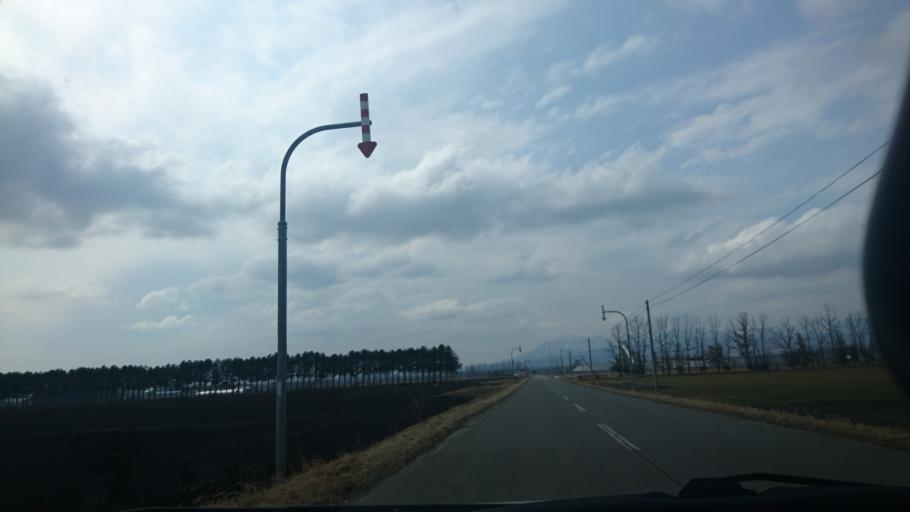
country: JP
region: Hokkaido
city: Otofuke
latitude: 43.2156
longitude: 143.2866
